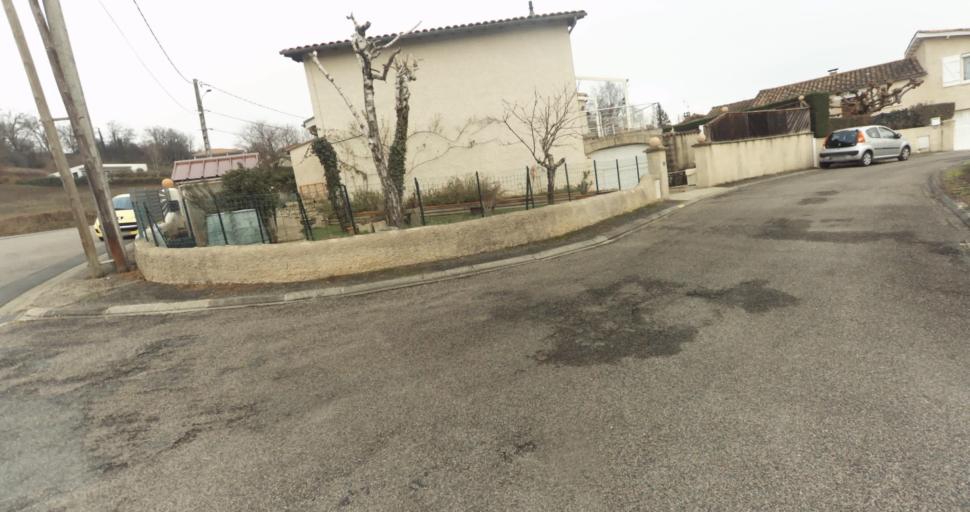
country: FR
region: Midi-Pyrenees
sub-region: Departement du Lot
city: Figeac
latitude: 44.6136
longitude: 2.0229
